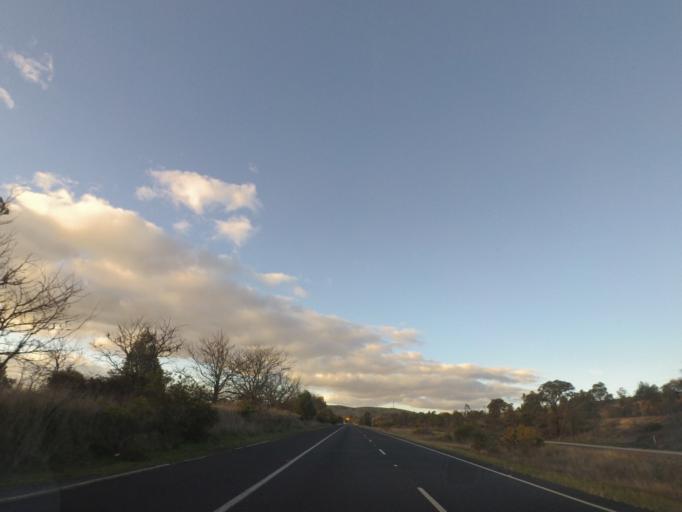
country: AU
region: New South Wales
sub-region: Yass Valley
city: Yass
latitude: -34.7875
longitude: 148.7014
